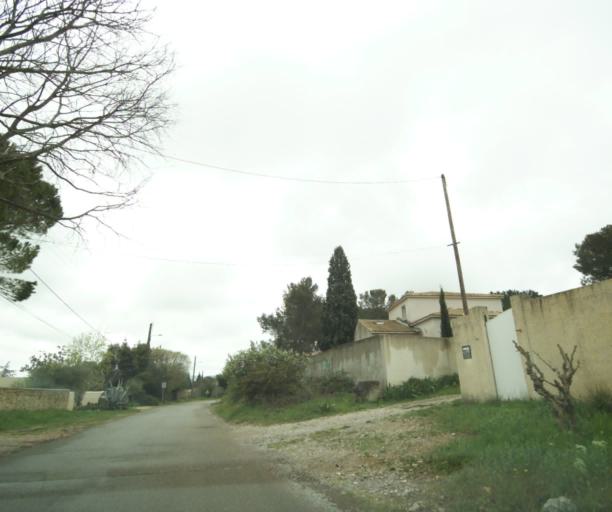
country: FR
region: Languedoc-Roussillon
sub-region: Departement de l'Herault
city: Cournonsec
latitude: 43.5597
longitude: 3.7091
